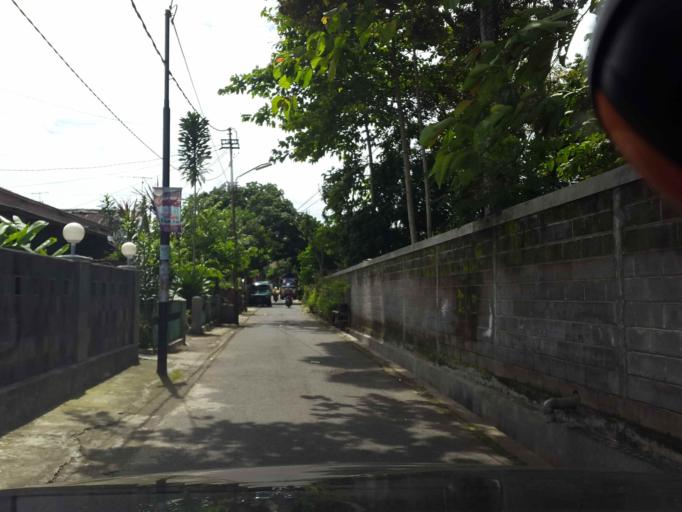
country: ID
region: Central Java
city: Salatiga
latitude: -7.3300
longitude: 110.4937
